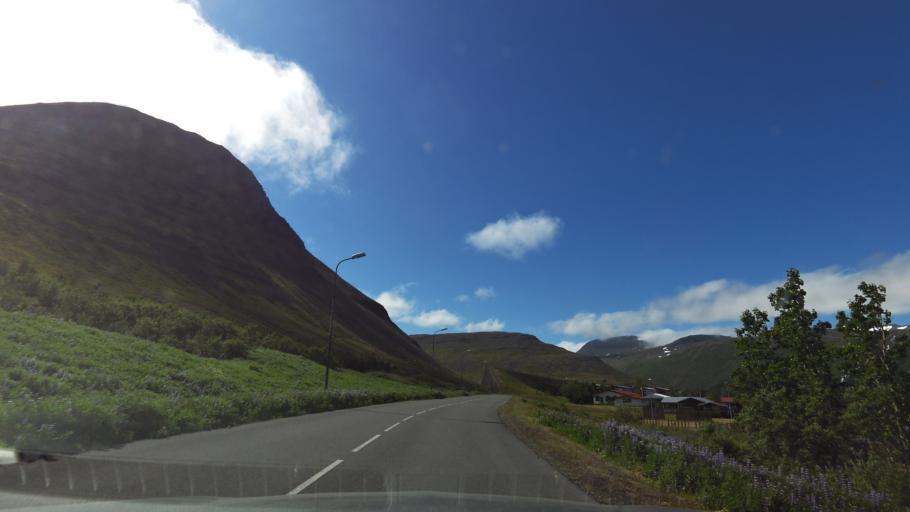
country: IS
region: Westfjords
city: Isafjoerdur
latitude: 66.0544
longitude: -23.1694
